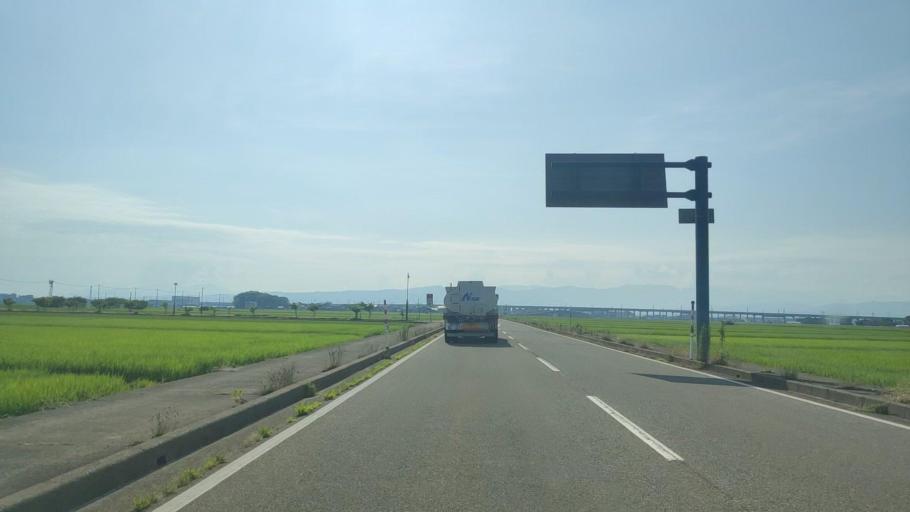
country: JP
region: Ishikawa
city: Matsuto
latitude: 36.5004
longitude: 136.5066
